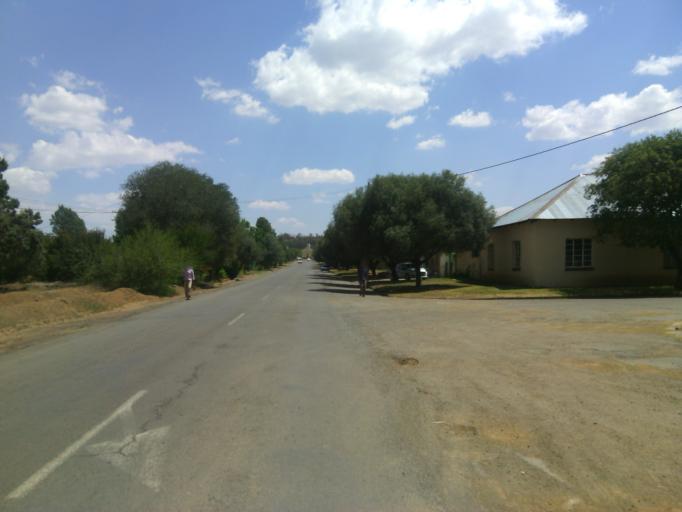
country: ZA
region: Orange Free State
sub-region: Xhariep District Municipality
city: Dewetsdorp
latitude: -29.5805
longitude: 26.6699
